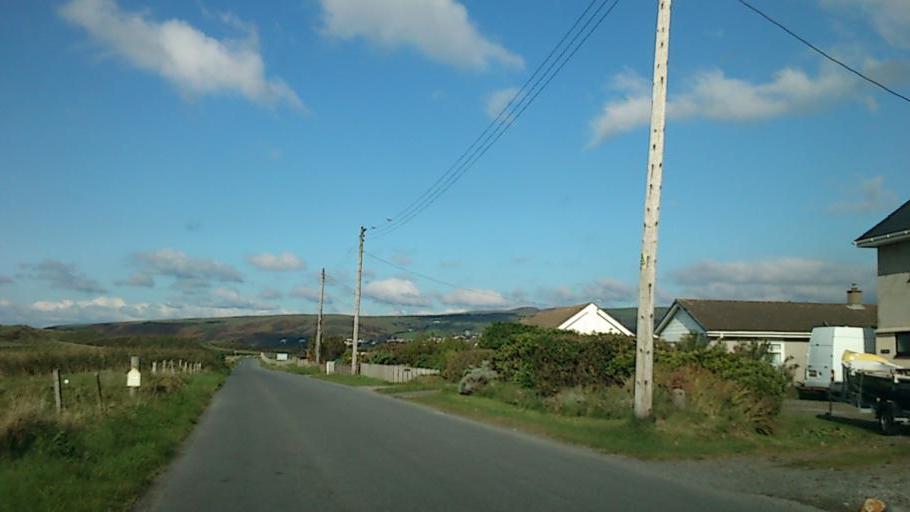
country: GB
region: Wales
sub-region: Gwynedd
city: Tywyn
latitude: 52.5180
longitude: -4.0535
